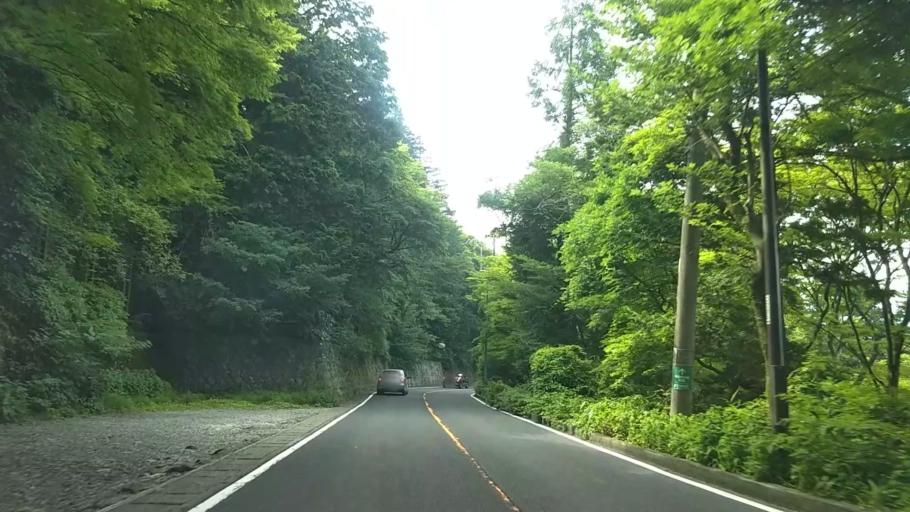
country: JP
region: Kanagawa
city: Hakone
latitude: 35.2343
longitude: 139.0485
